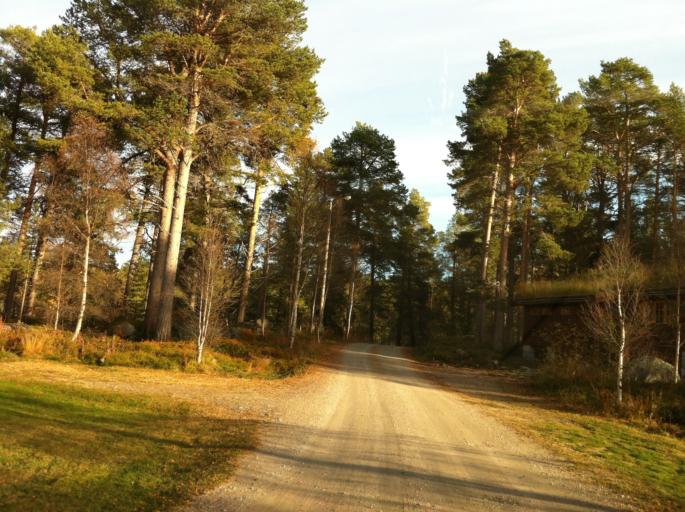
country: NO
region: Hedmark
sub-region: Engerdal
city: Engerdal
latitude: 62.1711
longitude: 11.9420
